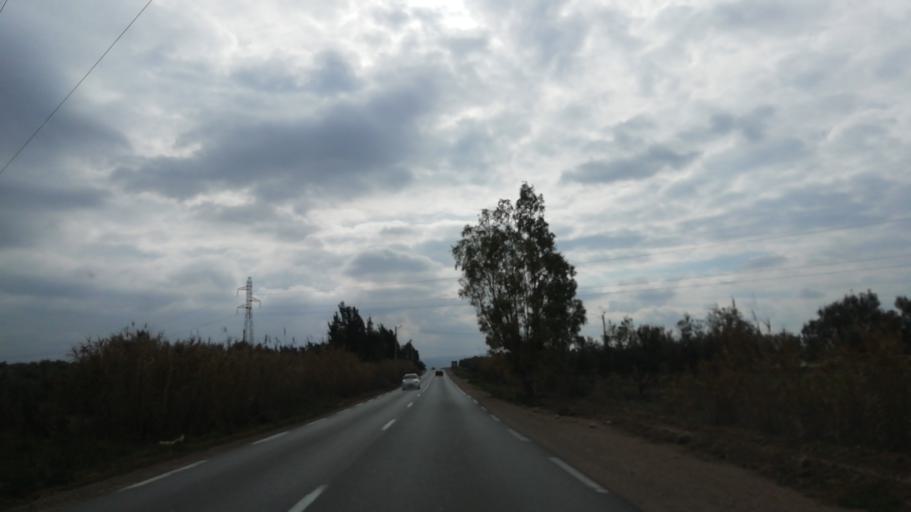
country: DZ
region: Oran
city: Sidi ech Chahmi
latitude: 35.5737
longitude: -0.4511
